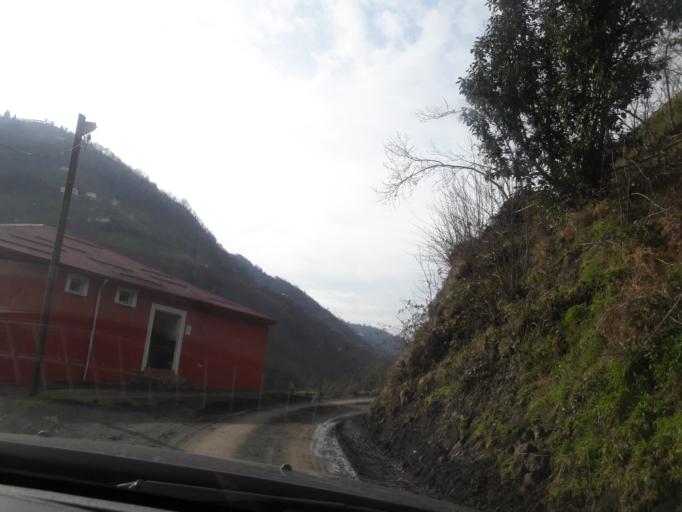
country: TR
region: Trabzon
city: Salpazari
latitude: 40.9702
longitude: 39.1965
